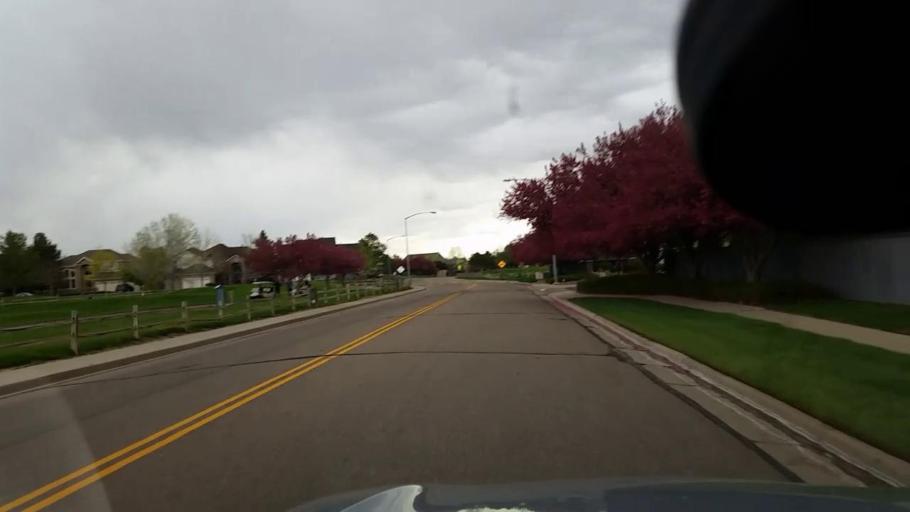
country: US
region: Colorado
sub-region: Adams County
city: Northglenn
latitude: 39.9395
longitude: -104.9723
